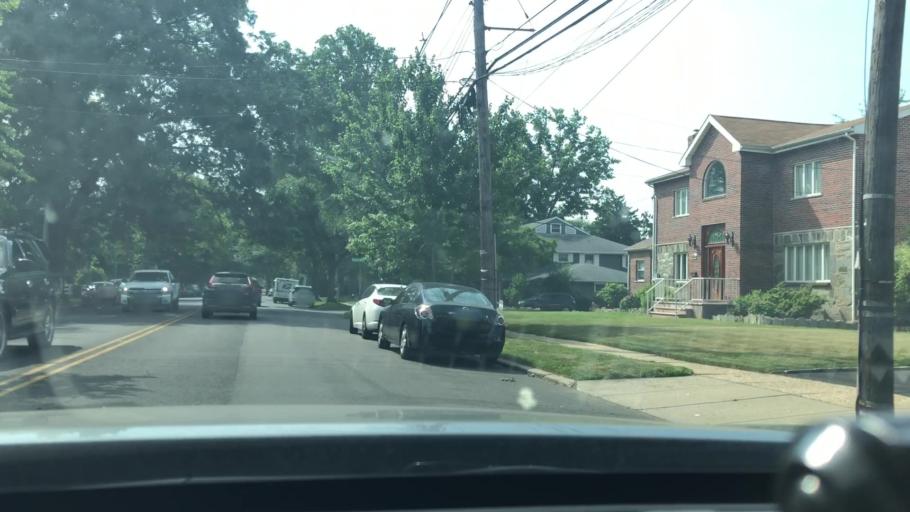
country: US
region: New Jersey
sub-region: Union County
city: Winfield
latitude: 40.6431
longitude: -74.2722
